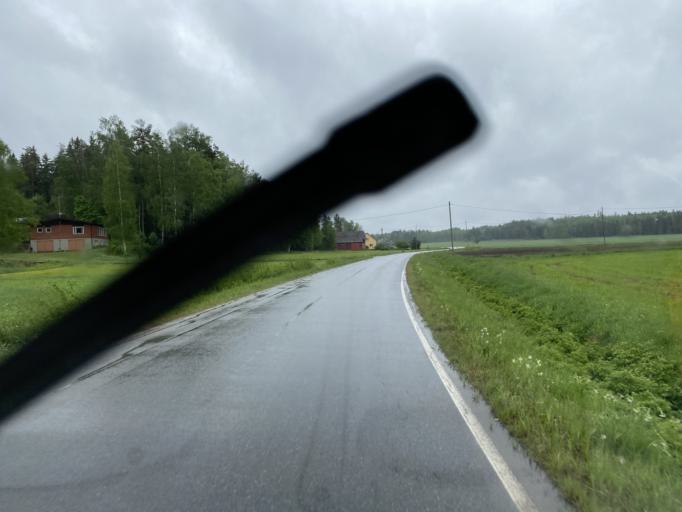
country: FI
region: Haeme
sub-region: Forssa
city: Humppila
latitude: 61.0490
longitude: 23.3667
